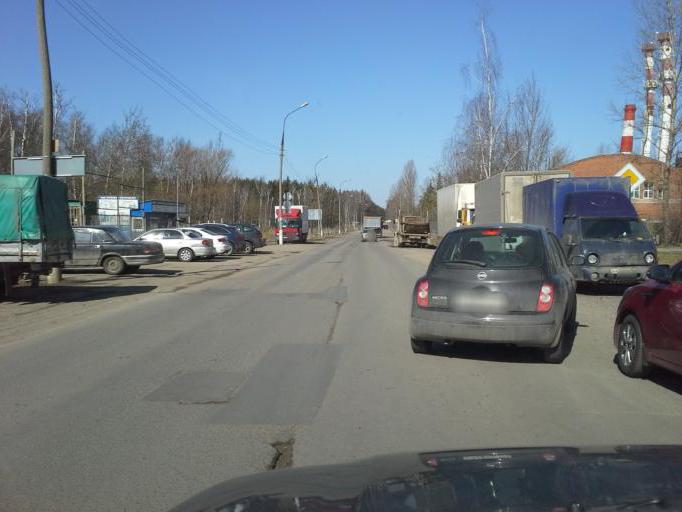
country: RU
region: Moskovskaya
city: Kokoshkino
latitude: 55.6020
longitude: 37.1640
